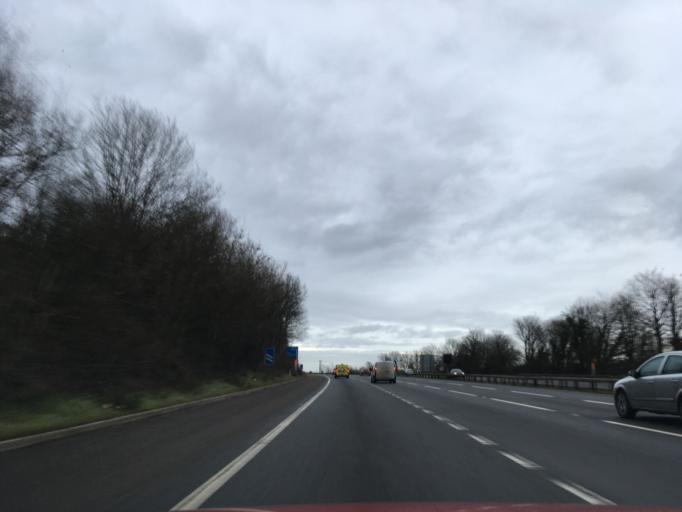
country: GB
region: Wales
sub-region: Cardiff
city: Pentyrch
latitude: 51.5070
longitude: -3.3241
